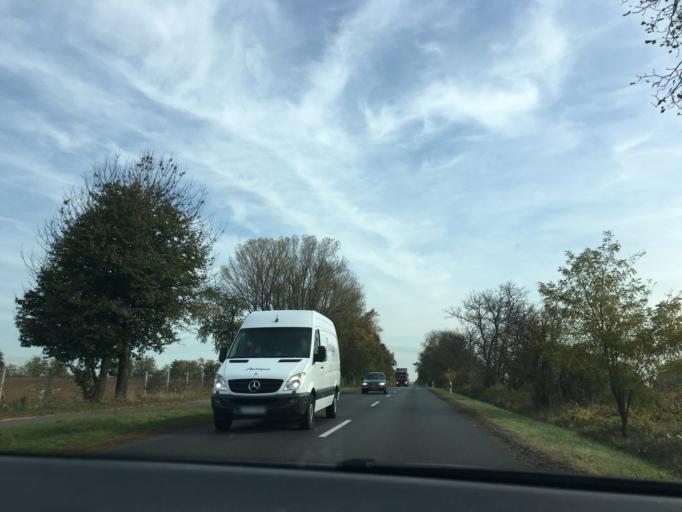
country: HU
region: Szabolcs-Szatmar-Bereg
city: Nagykallo
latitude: 47.8653
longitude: 21.8826
